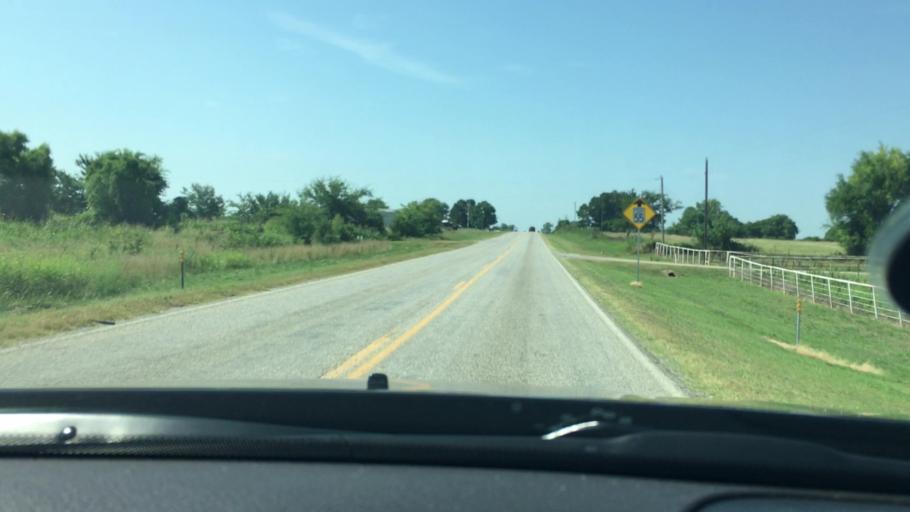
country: US
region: Oklahoma
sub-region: Johnston County
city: Tishomingo
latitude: 34.2816
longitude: -96.4248
